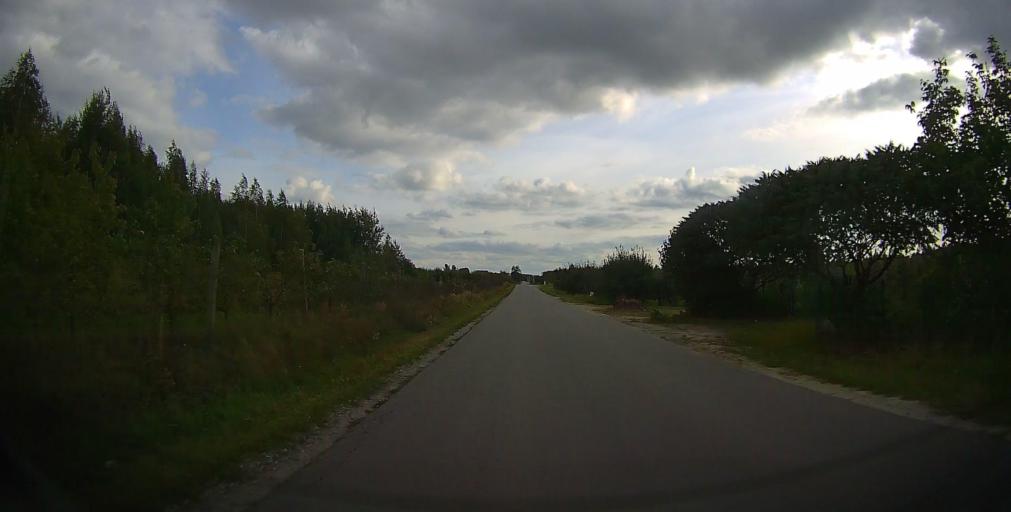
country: PL
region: Masovian Voivodeship
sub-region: Powiat bialobrzeski
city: Promna
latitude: 51.7166
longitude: 20.9584
